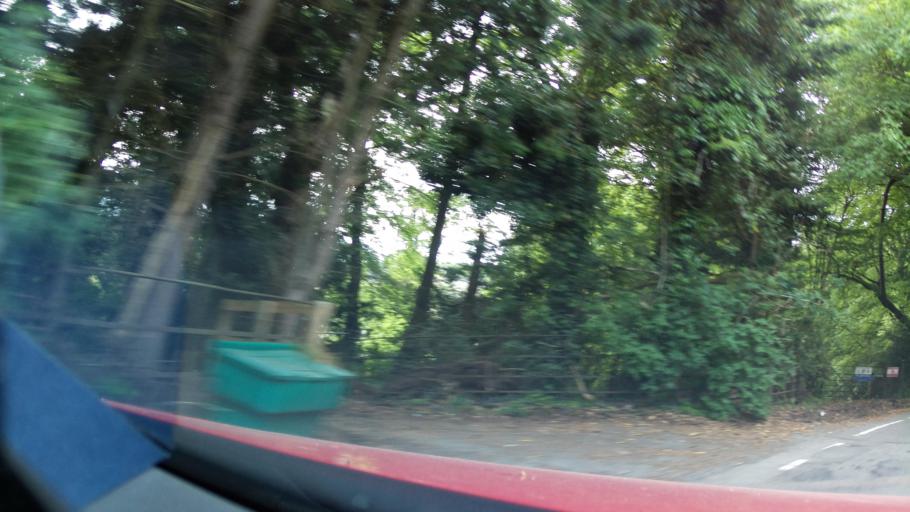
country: GB
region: England
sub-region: Gloucestershire
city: Shurdington
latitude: 51.8487
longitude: -2.0810
